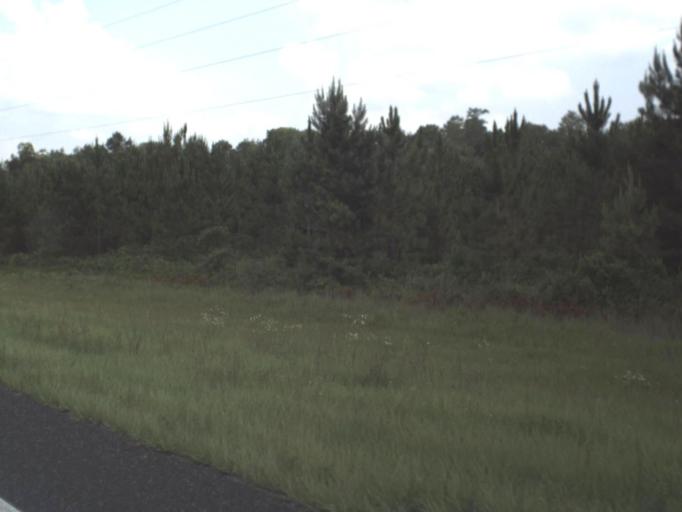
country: US
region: Florida
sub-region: Levy County
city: Bronson
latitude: 29.4768
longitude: -82.6902
